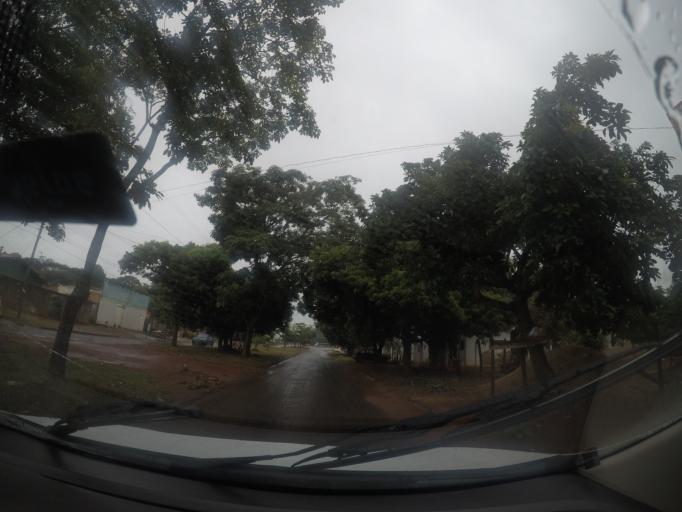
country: BR
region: Goias
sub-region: Trindade
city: Trindade
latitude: -16.6450
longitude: -49.4341
